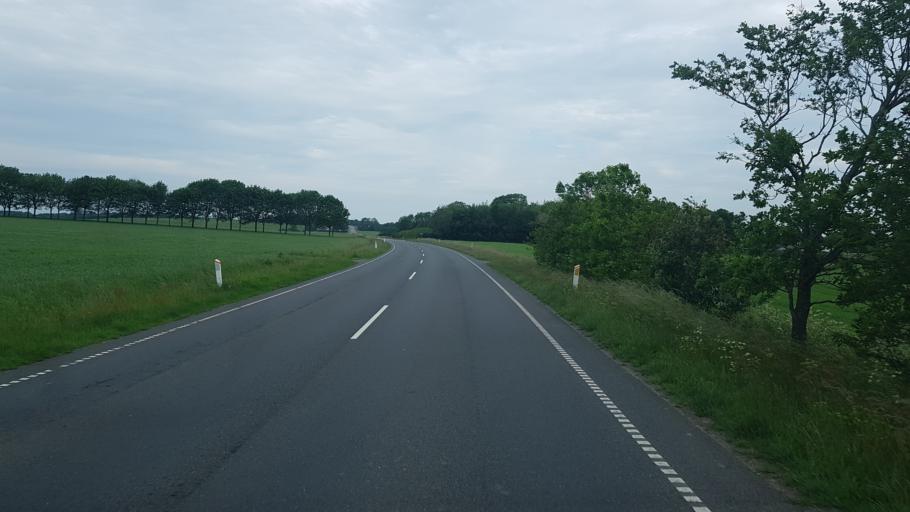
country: DK
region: South Denmark
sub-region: Vejen Kommune
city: Rodding
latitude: 55.4087
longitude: 9.0323
